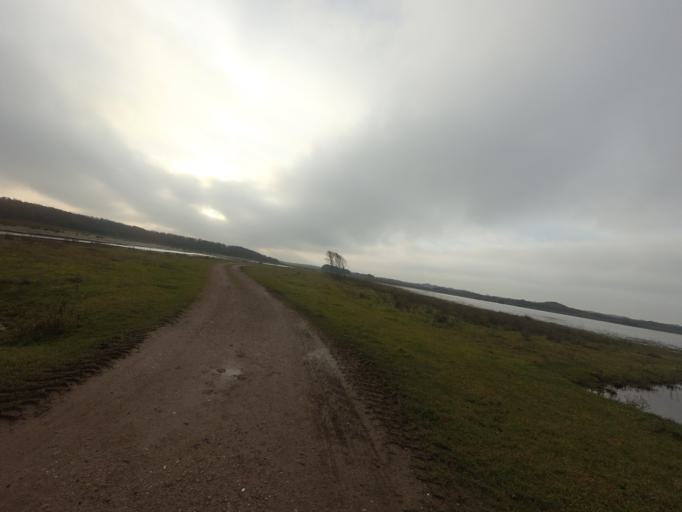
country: NL
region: North Holland
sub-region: Gemeente Texel
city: Den Burg
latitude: 53.1179
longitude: 4.7950
